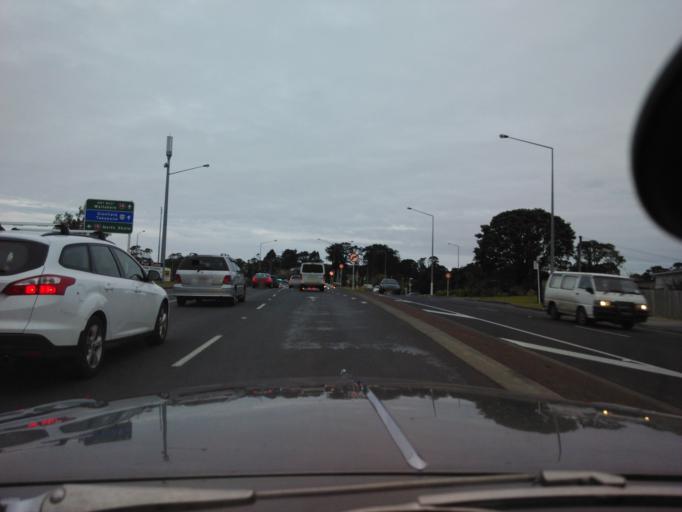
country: NZ
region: Auckland
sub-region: Auckland
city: Rothesay Bay
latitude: -36.7563
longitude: 174.7023
